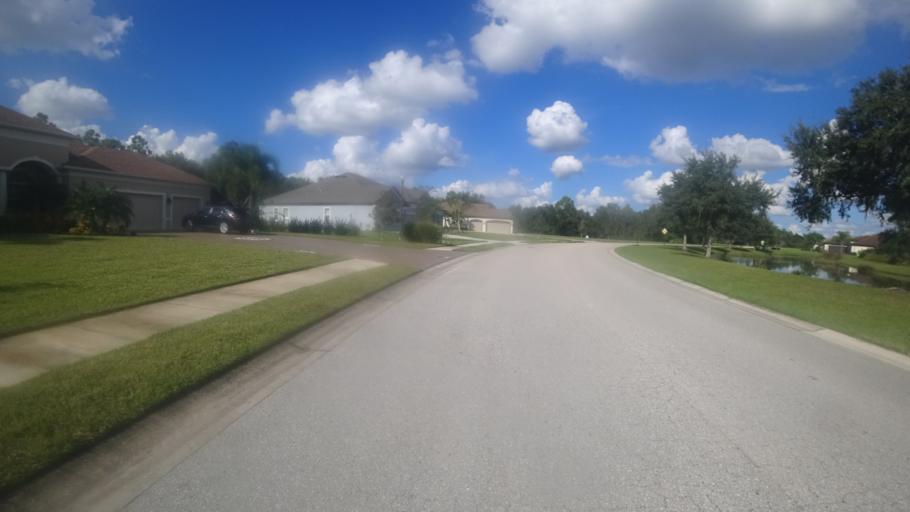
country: US
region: Florida
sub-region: Manatee County
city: Ellenton
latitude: 27.5380
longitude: -82.3820
